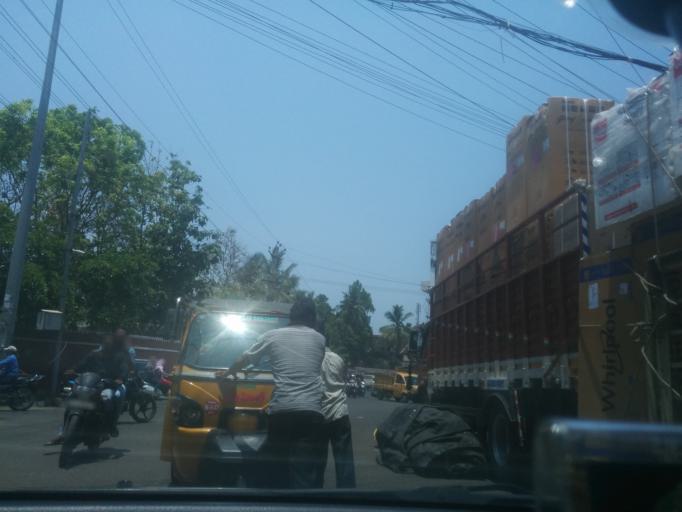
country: IN
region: Andhra Pradesh
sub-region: East Godavari
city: Rajahmundry
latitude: 16.9967
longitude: 81.7754
